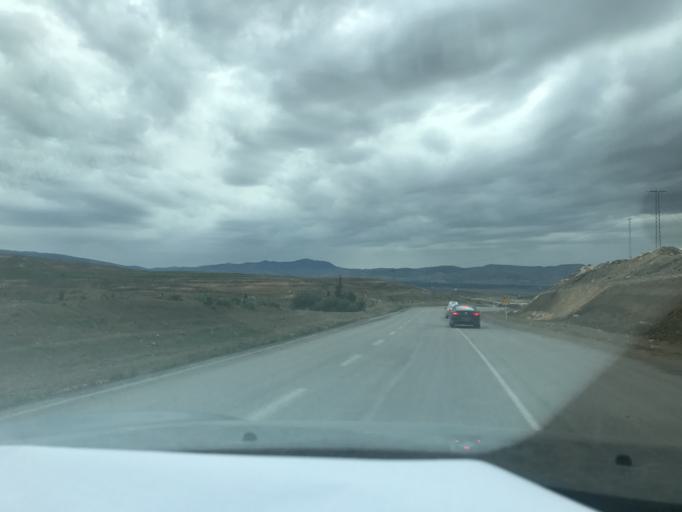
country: TN
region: Silyanah
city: Siliana
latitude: 36.0913
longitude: 9.4676
